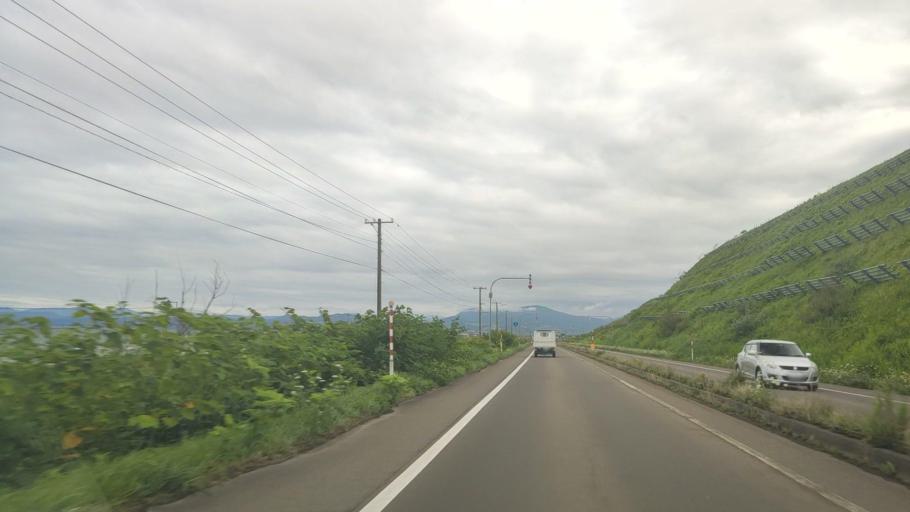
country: JP
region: Hokkaido
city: Niseko Town
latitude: 42.3278
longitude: 140.2770
